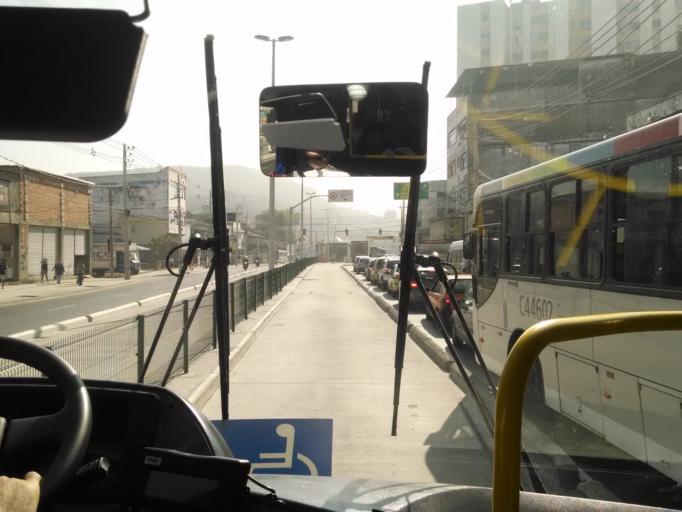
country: BR
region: Rio de Janeiro
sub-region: Sao Joao De Meriti
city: Sao Joao de Meriti
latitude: -22.8675
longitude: -43.3347
